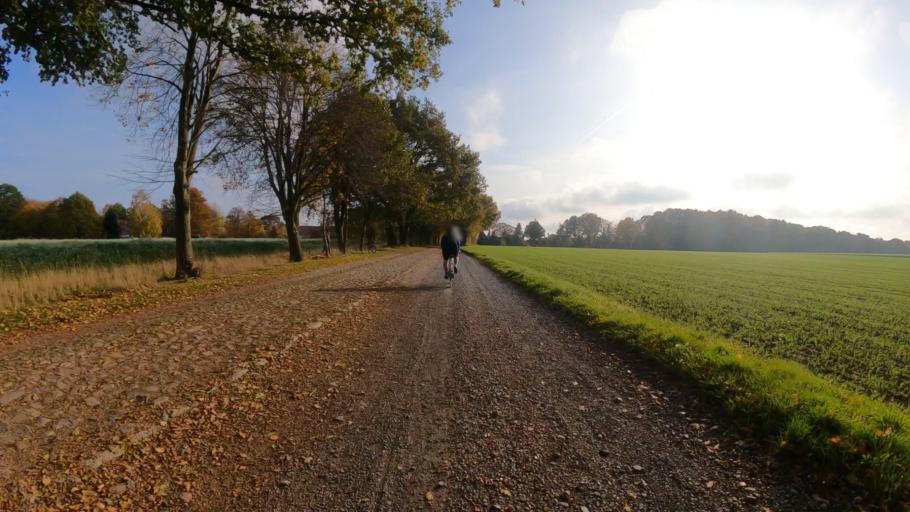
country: DE
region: Lower Saxony
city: Buchholz in der Nordheide
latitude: 53.3352
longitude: 9.8381
